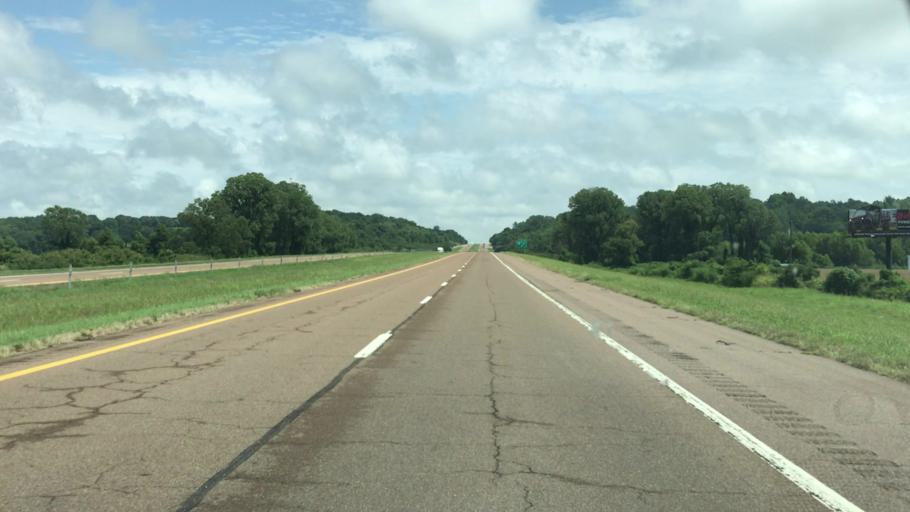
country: US
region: Tennessee
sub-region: Dyer County
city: Dyersburg
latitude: 36.0765
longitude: -89.5058
